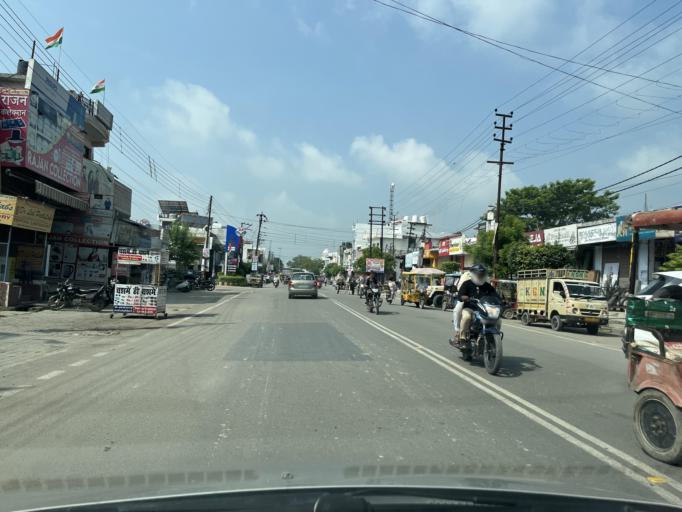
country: IN
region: Uttarakhand
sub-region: Udham Singh Nagar
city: Bazpur
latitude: 29.1594
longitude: 79.1518
